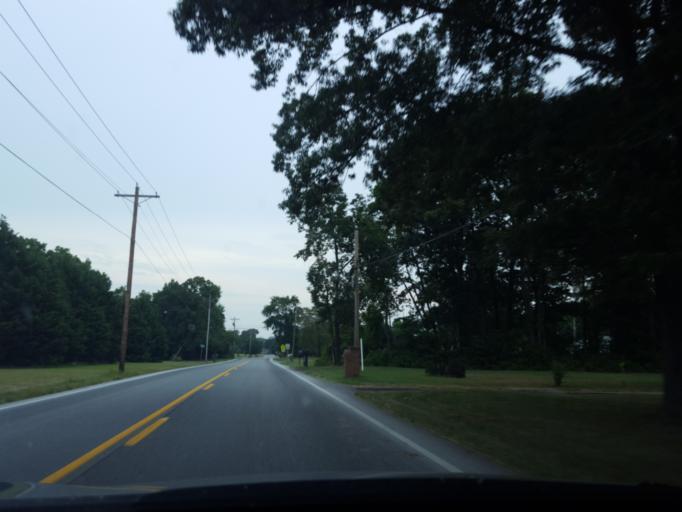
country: US
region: Maryland
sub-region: Saint Mary's County
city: Charlotte Hall
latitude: 38.4645
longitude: -76.7798
